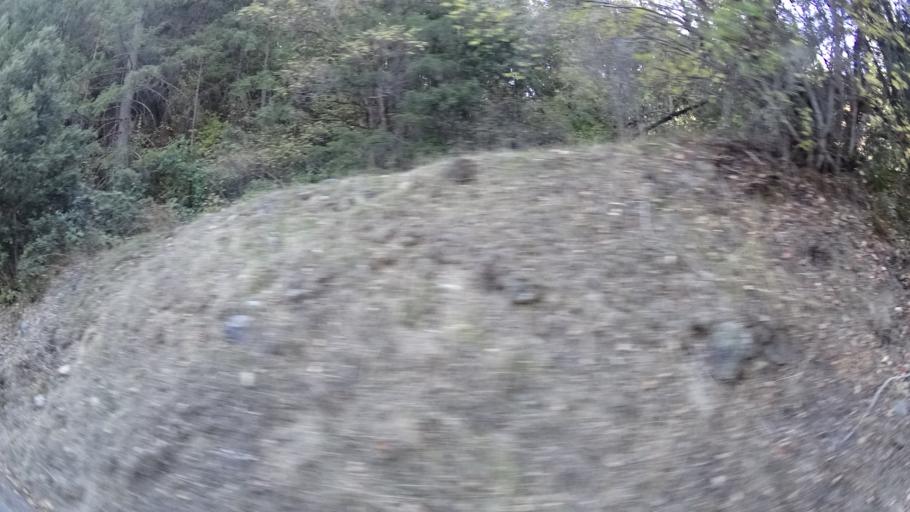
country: US
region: California
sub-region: Humboldt County
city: Willow Creek
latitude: 41.2533
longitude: -123.3167
